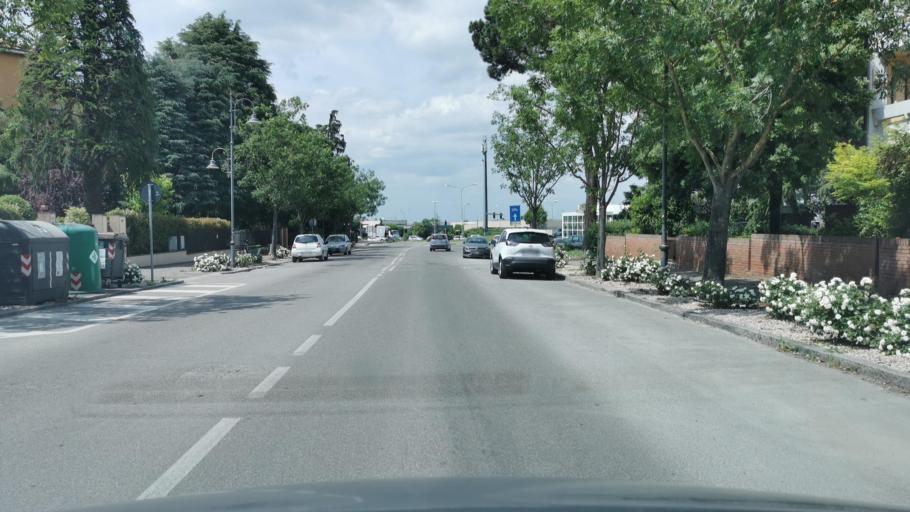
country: IT
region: Emilia-Romagna
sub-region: Provincia di Bologna
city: Castel San Pietro Terme
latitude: 44.4015
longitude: 11.5874
